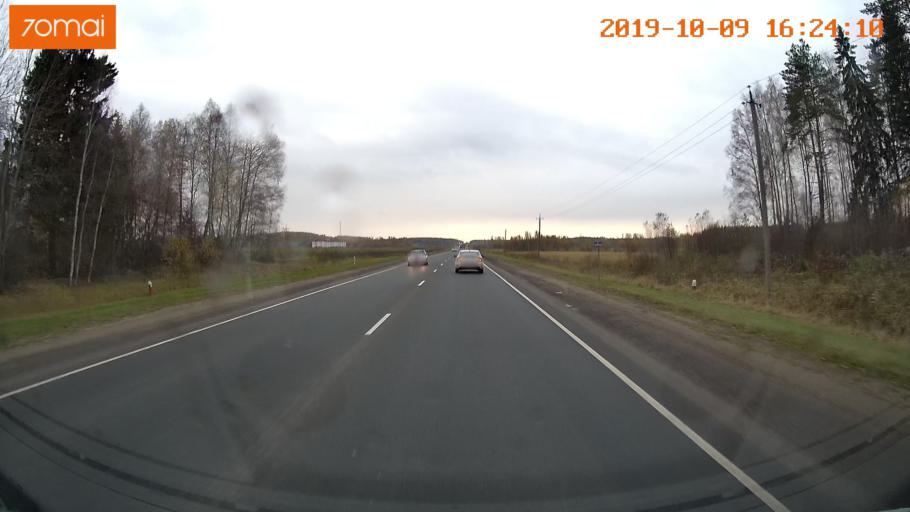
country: RU
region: Kostroma
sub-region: Kostromskoy Rayon
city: Kostroma
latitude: 57.6553
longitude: 40.9078
